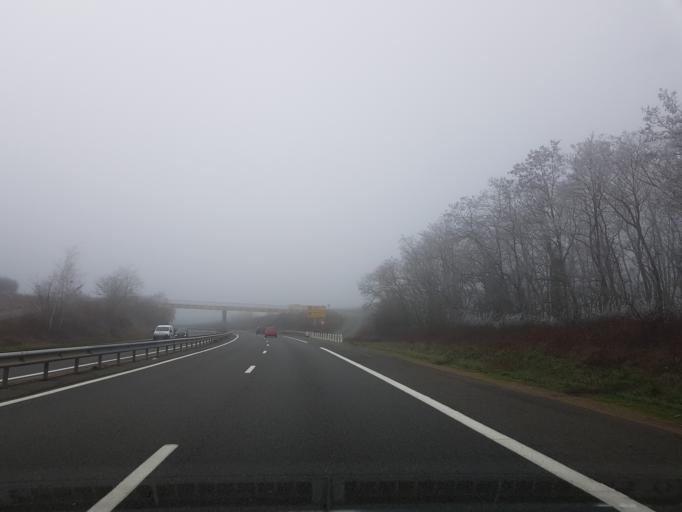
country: FR
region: Bourgogne
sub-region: Departement de Saone-et-Loire
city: Ecuisses
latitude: 46.7432
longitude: 4.5478
